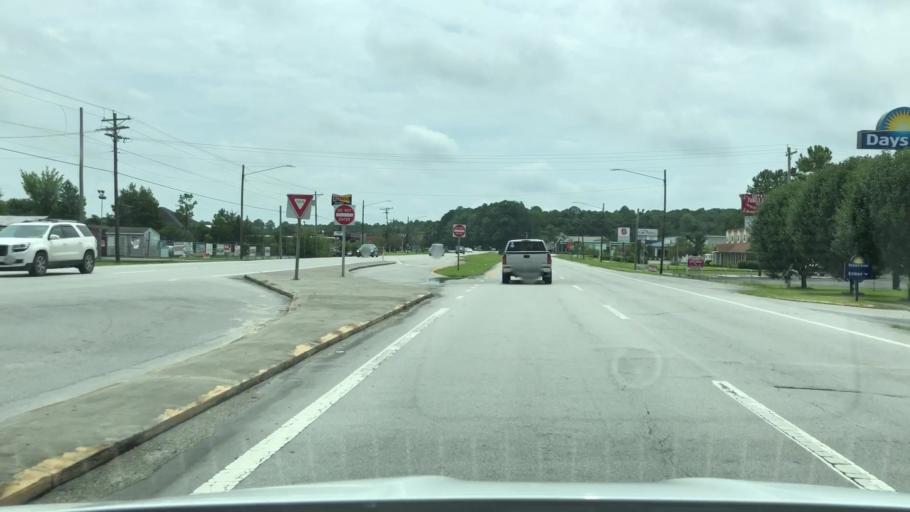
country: US
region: North Carolina
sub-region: Craven County
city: Havelock
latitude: 34.8607
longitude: -76.8975
